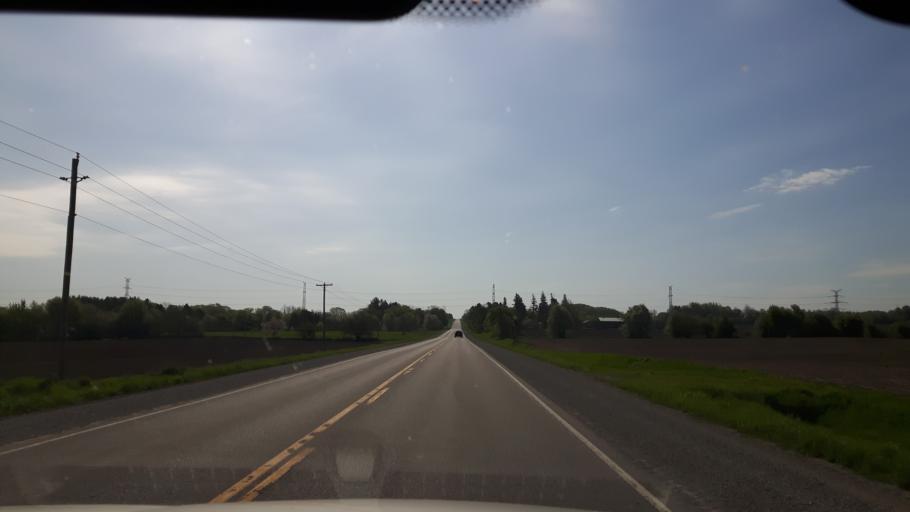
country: CA
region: Ontario
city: Bluewater
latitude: 43.5460
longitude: -81.6472
